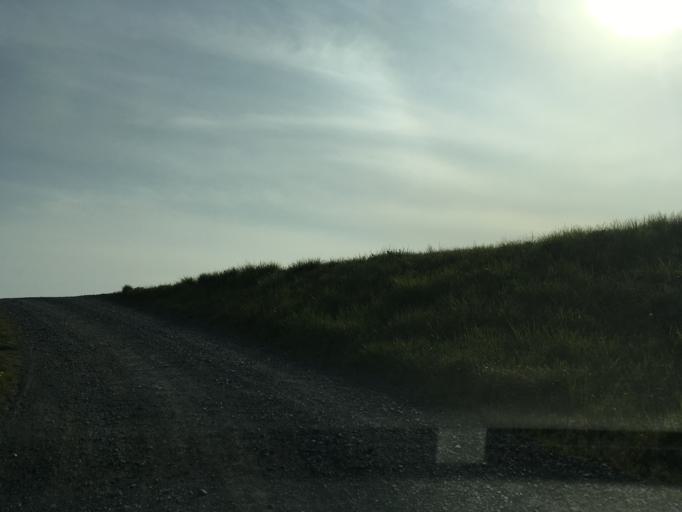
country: JP
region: Miyagi
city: Wakuya
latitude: 38.7215
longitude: 141.2703
